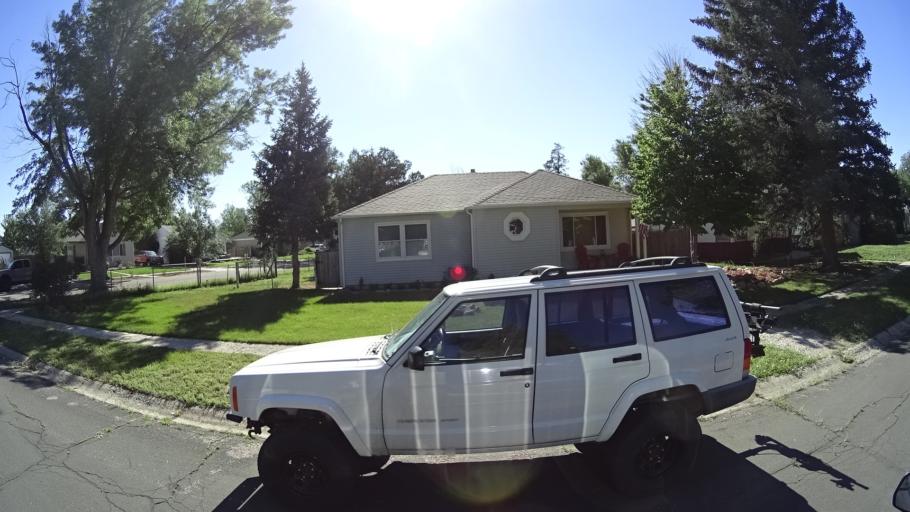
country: US
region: Colorado
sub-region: El Paso County
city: Colorado Springs
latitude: 38.8695
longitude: -104.8157
